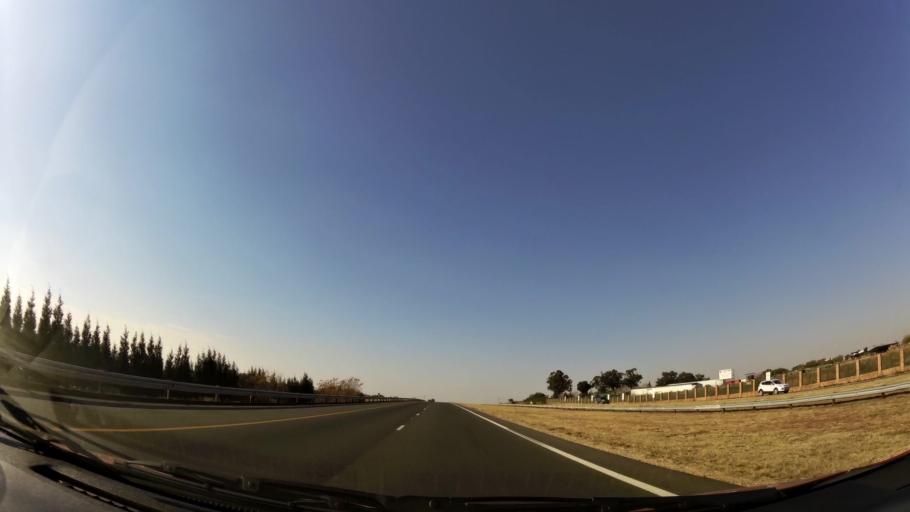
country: ZA
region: Gauteng
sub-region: West Rand District Municipality
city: Muldersdriseloop
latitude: -25.9920
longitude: 27.9133
